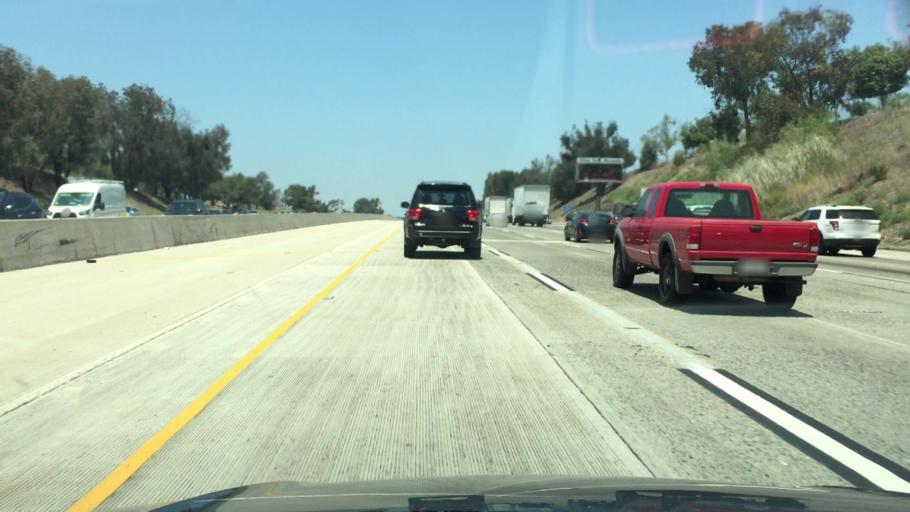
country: US
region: California
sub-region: Orange County
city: San Juan Capistrano
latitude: 33.5125
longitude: -117.6623
